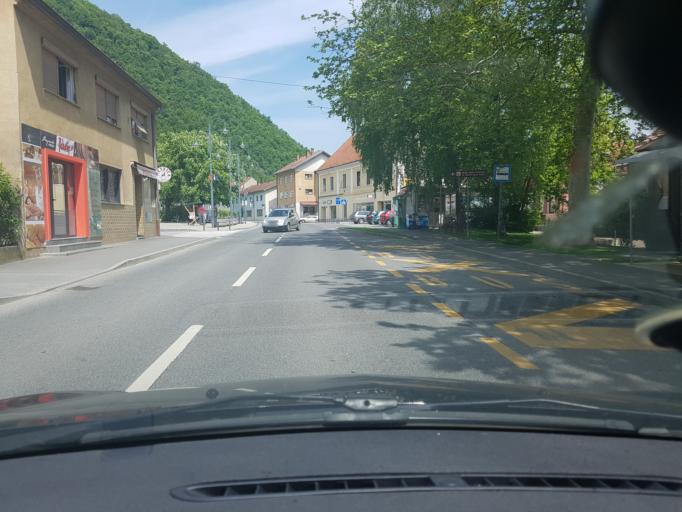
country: HR
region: Krapinsko-Zagorska
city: Pregrada
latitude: 46.1642
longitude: 15.7504
